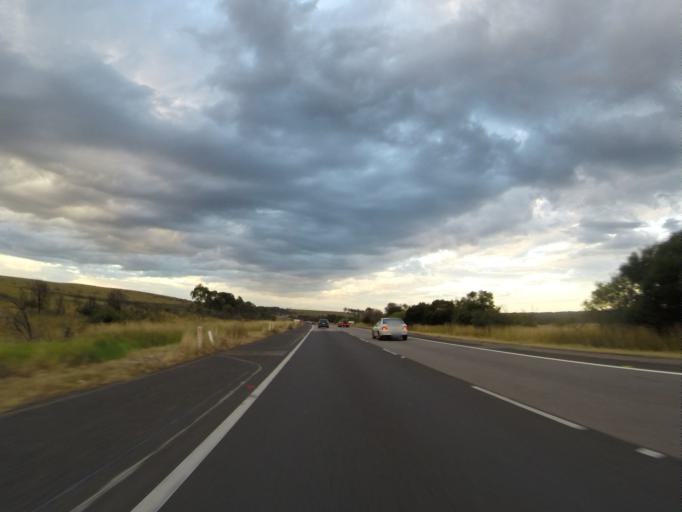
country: AU
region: New South Wales
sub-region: Wollondilly
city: Douglas Park
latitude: -34.1713
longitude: 150.7330
